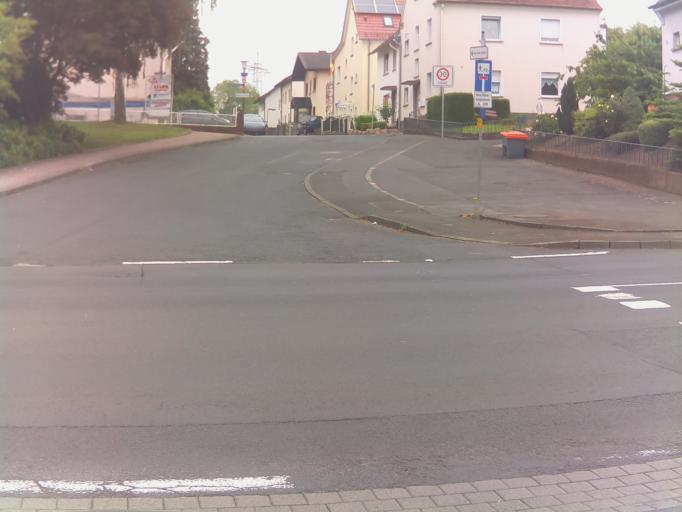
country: DE
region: Hesse
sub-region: Regierungsbezirk Kassel
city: Fulda
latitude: 50.5261
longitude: 9.6792
